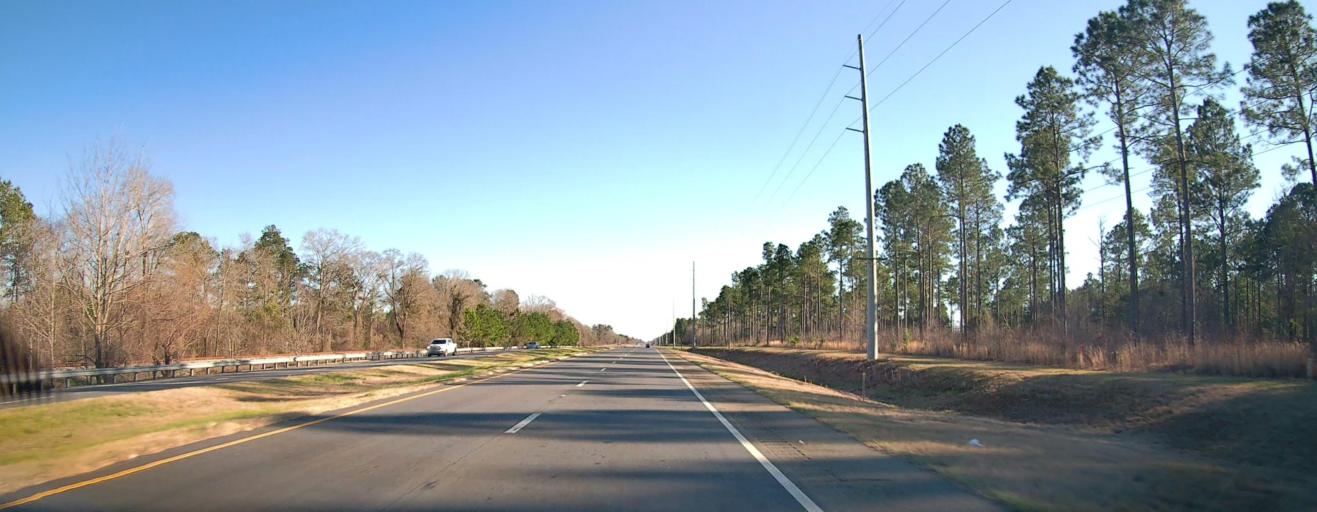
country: US
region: Georgia
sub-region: Lee County
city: Leesburg
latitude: 31.8724
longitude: -84.2388
